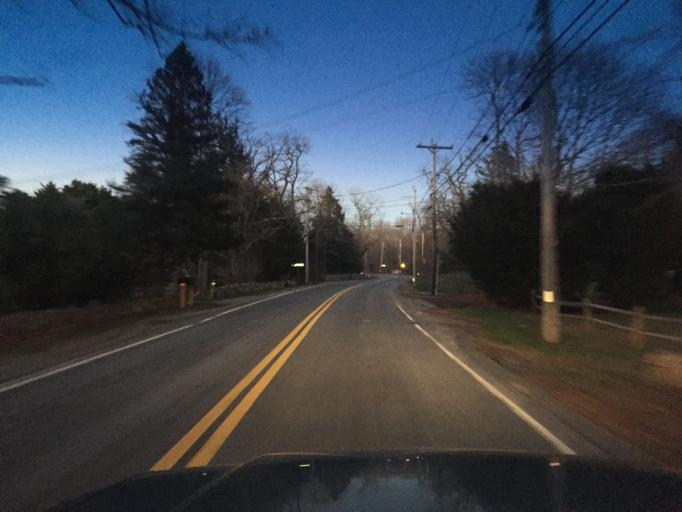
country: US
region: Massachusetts
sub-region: Barnstable County
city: North Falmouth
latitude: 41.6293
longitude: -70.6200
